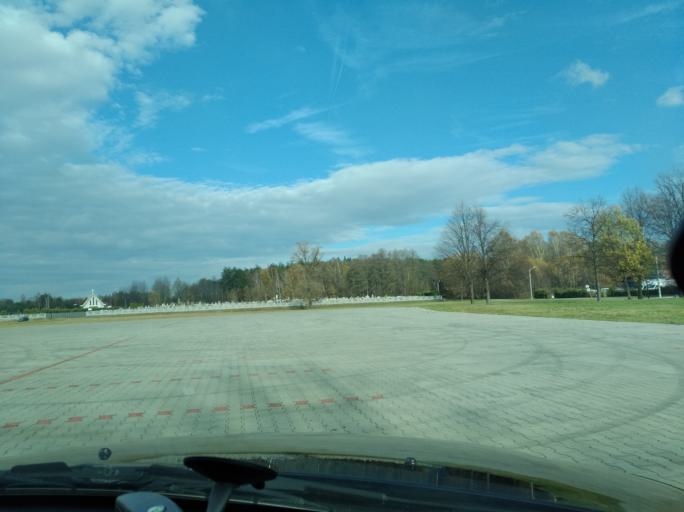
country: PL
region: Subcarpathian Voivodeship
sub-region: Powiat ropczycko-sedziszowski
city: Sedziszow Malopolski
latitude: 50.1161
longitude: 21.7353
